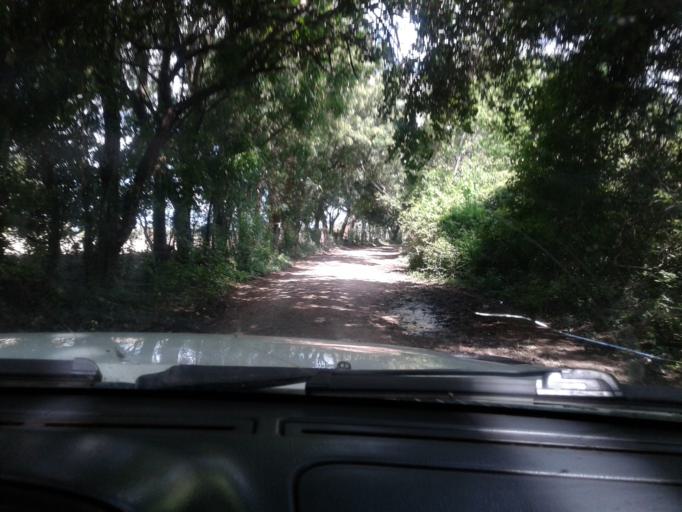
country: NI
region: Matagalpa
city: Ciudad Dario
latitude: 12.8453
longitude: -86.1245
